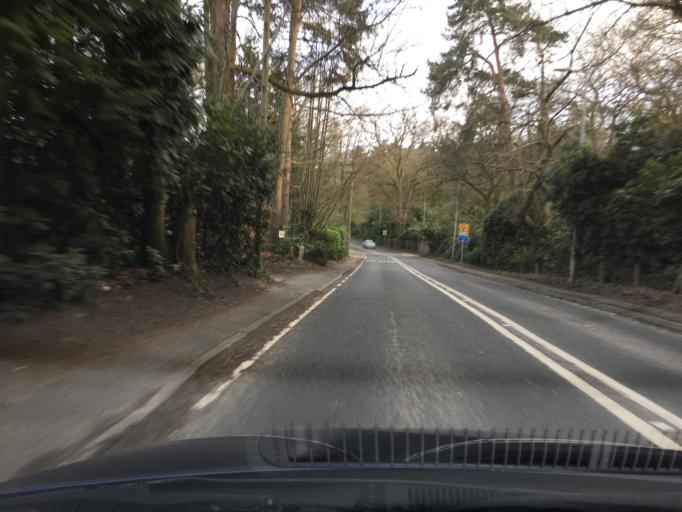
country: GB
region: England
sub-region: Hampshire
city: Yateley
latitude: 51.3610
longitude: -0.8195
